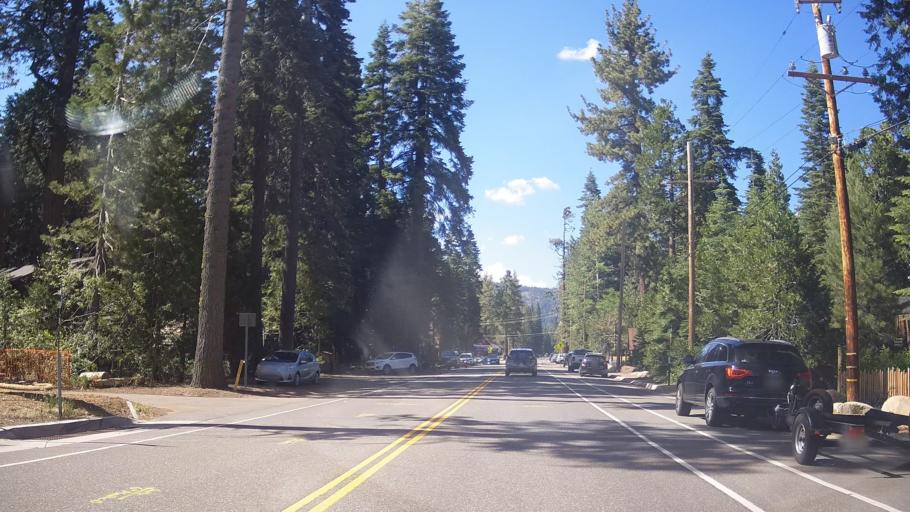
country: US
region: California
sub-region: Placer County
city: Tahoma
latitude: 39.0830
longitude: -120.1589
